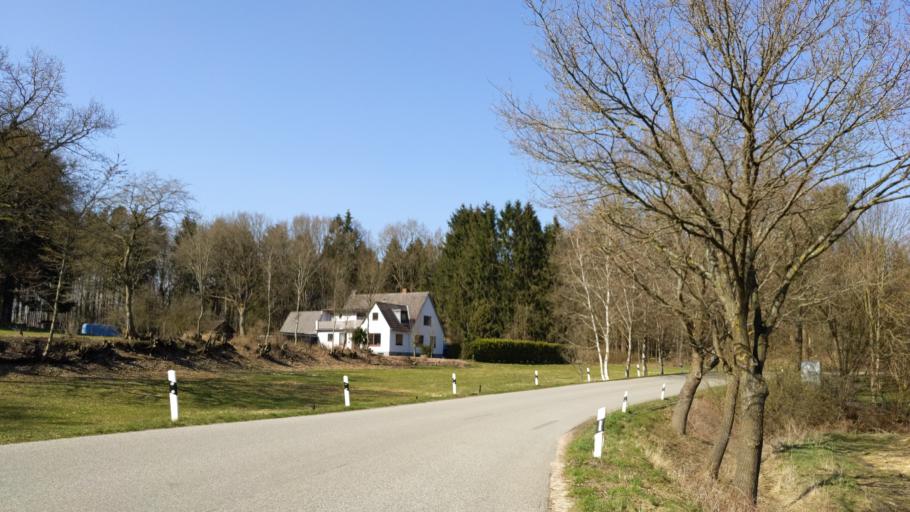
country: DE
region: Schleswig-Holstein
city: Susel
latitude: 54.0941
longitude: 10.7081
